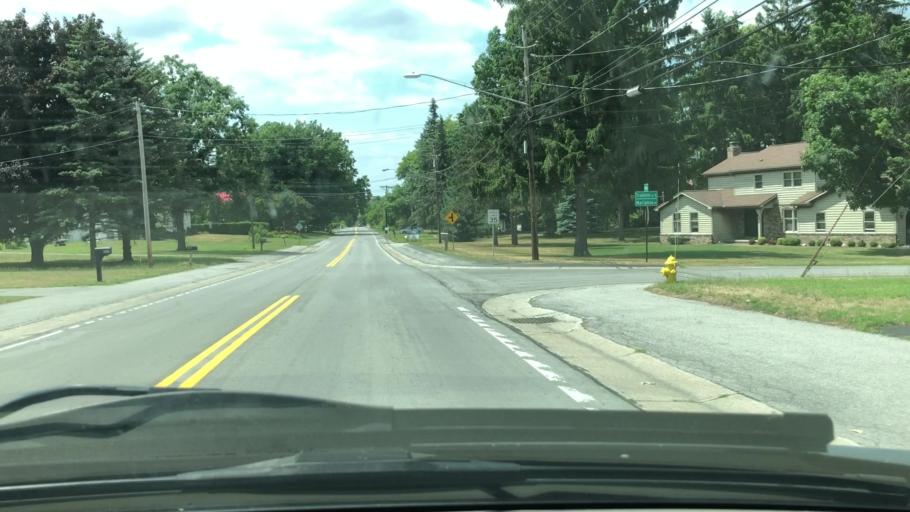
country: US
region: New York
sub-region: Monroe County
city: North Gates
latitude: 43.1256
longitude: -77.7253
